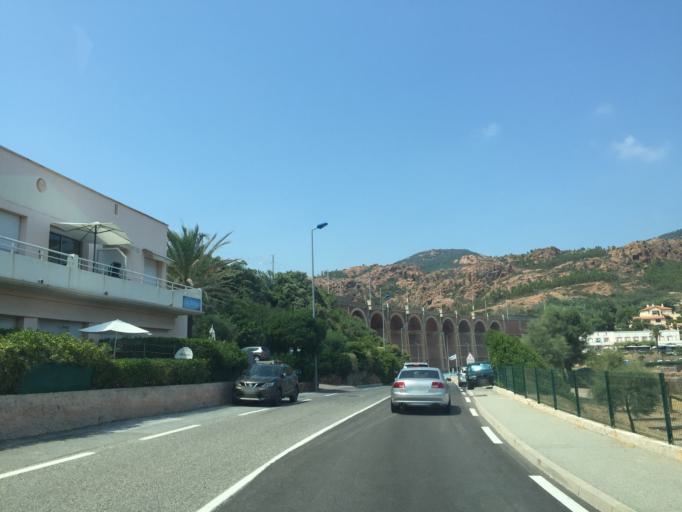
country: FR
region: Provence-Alpes-Cote d'Azur
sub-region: Departement des Alpes-Maritimes
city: Theoule-sur-Mer
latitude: 43.4356
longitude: 6.8926
